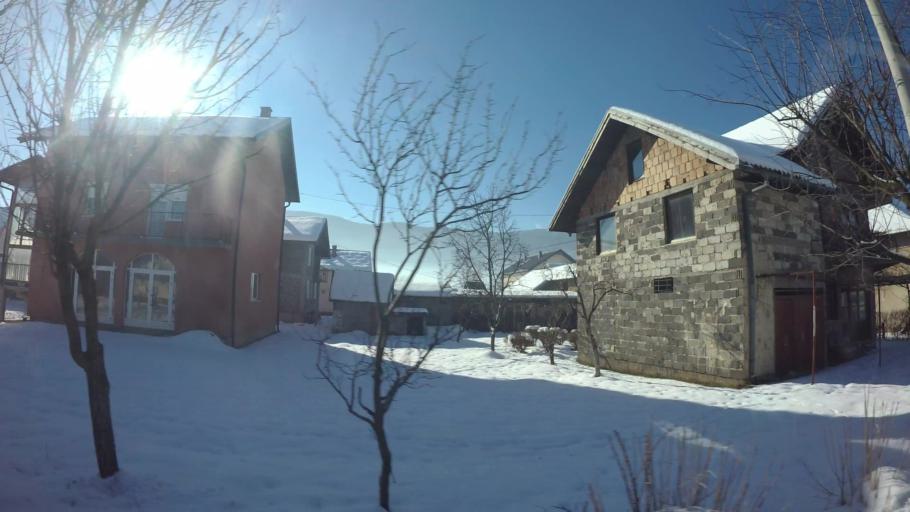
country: BA
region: Federation of Bosnia and Herzegovina
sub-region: Kanton Sarajevo
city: Sarajevo
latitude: 43.7973
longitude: 18.3404
